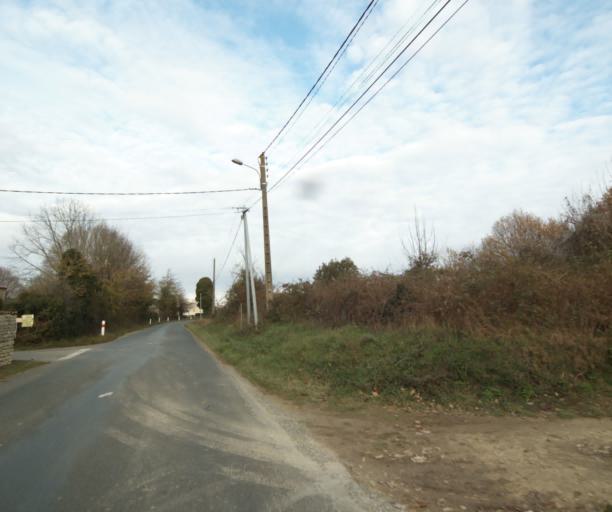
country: FR
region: Poitou-Charentes
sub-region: Departement de la Charente-Maritime
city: Corme-Royal
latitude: 45.7602
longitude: -0.7969
